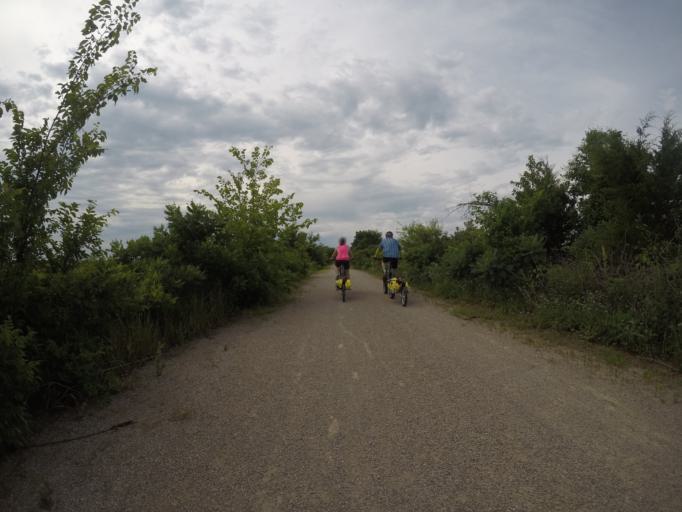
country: US
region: Kansas
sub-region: Anderson County
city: Garnett
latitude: 38.4451
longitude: -95.2652
